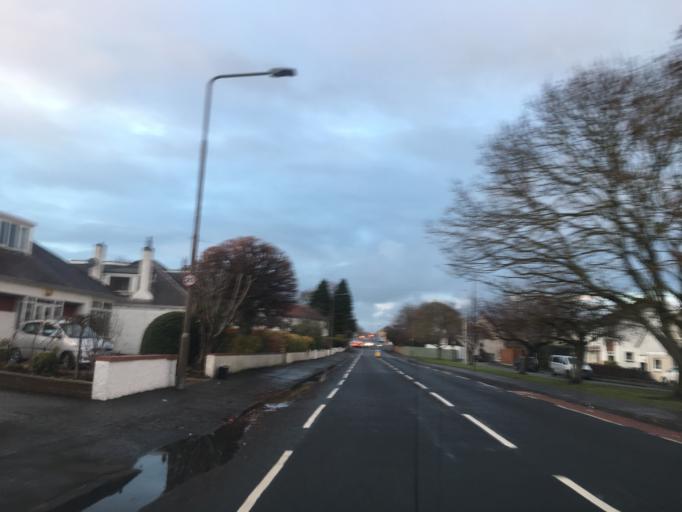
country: GB
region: Scotland
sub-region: Edinburgh
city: Colinton
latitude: 55.9608
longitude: -3.2712
